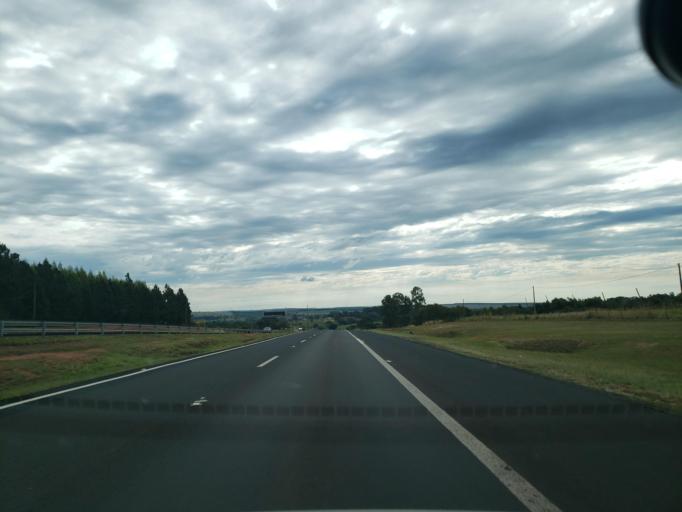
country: BR
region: Sao Paulo
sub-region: Bauru
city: Bauru
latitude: -22.2253
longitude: -49.1618
